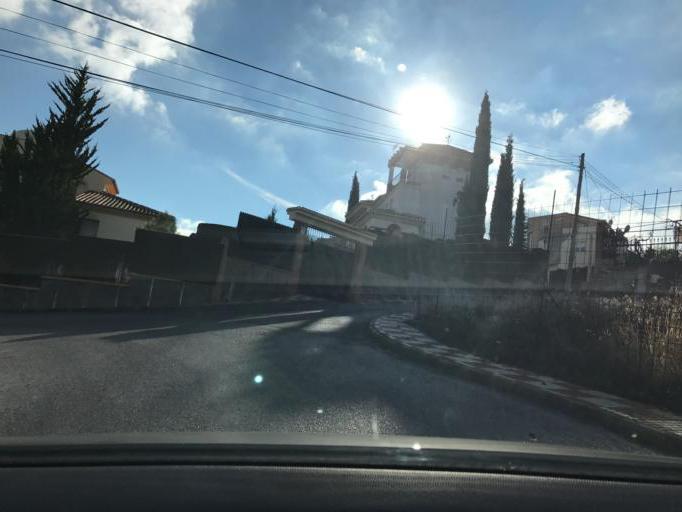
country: ES
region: Andalusia
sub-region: Provincia de Granada
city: Otura
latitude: 37.0853
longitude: -3.6290
